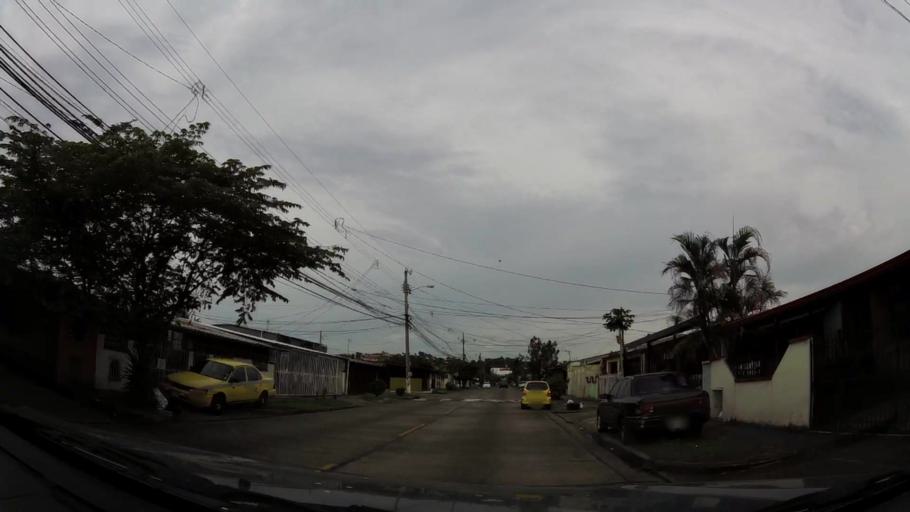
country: PA
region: Panama
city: San Miguelito
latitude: 9.0365
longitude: -79.4763
